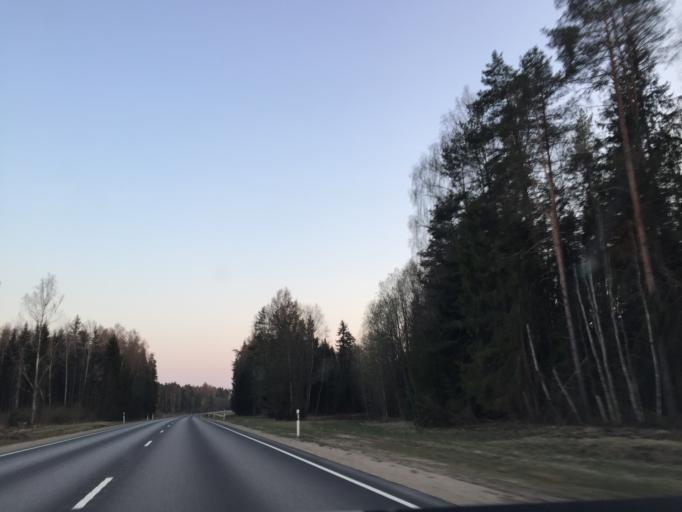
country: EE
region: Valgamaa
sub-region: Valga linn
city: Valga
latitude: 57.8898
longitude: 26.1655
